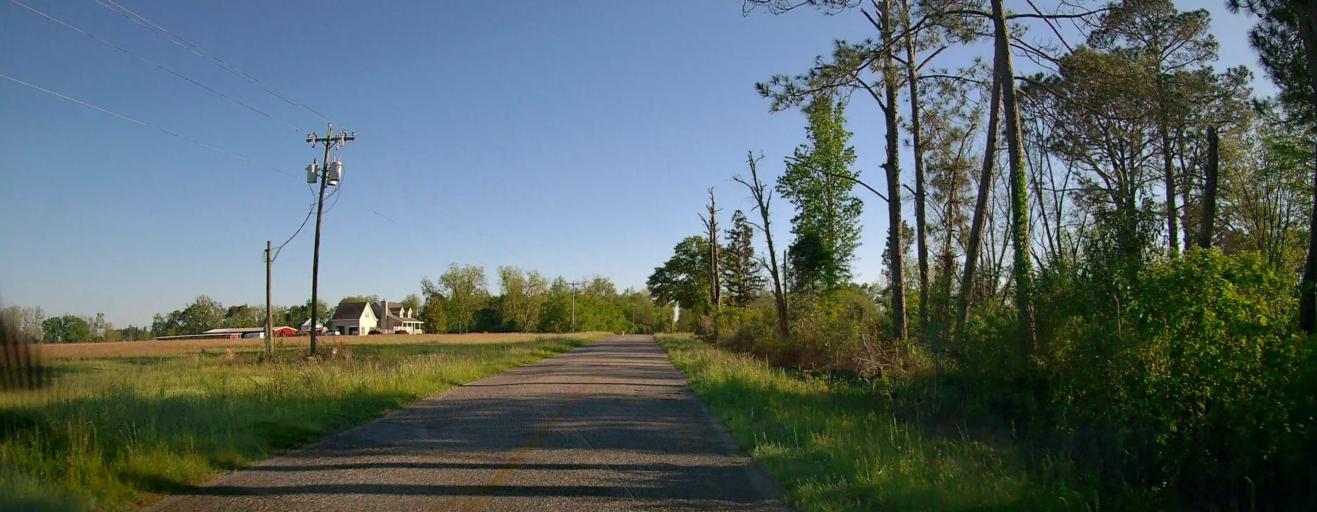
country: US
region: Georgia
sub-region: Ben Hill County
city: Fitzgerald
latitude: 31.6984
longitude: -83.1532
